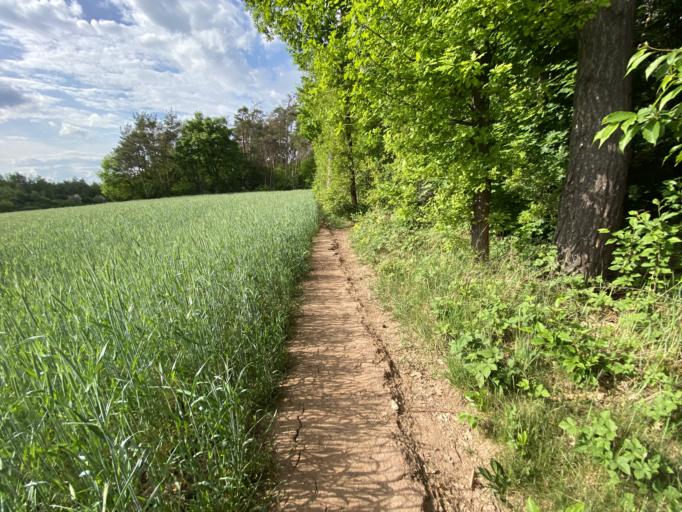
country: DE
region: Bavaria
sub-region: Regierungsbezirk Mittelfranken
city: Erlangen
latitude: 49.5565
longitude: 11.0120
